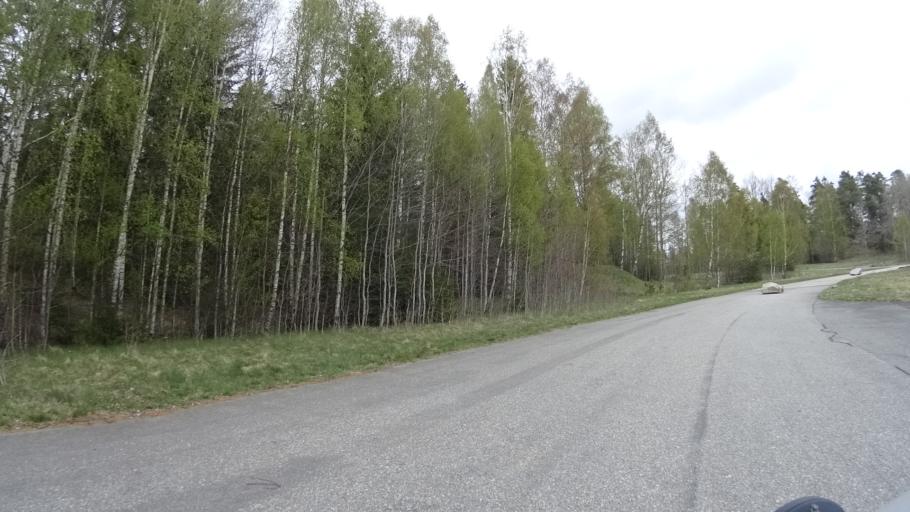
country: SE
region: Stockholm
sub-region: Botkyrka Kommun
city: Tullinge
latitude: 59.1767
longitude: 17.8908
